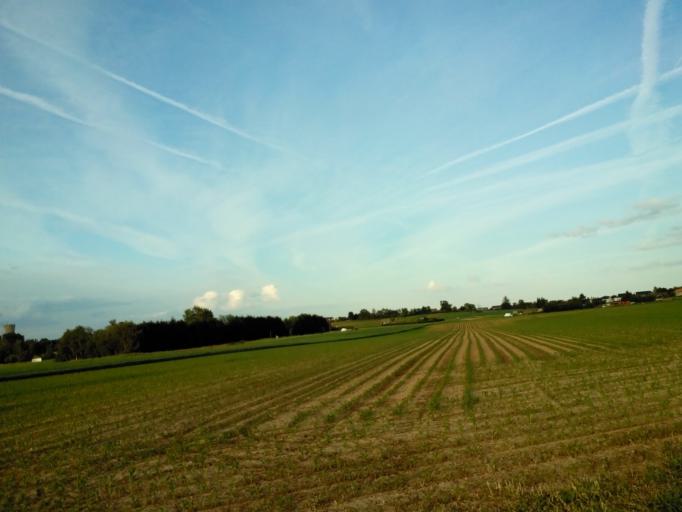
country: BE
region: Flanders
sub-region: Provincie Vlaams-Brabant
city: Bierbeek
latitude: 50.8394
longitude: 4.7183
